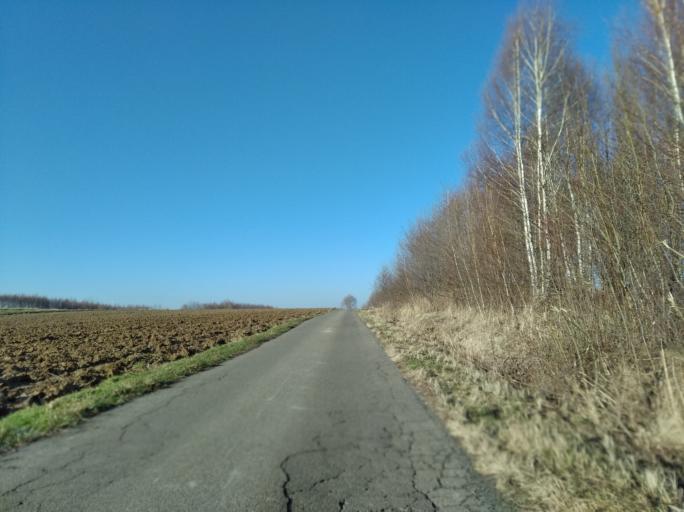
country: PL
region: Subcarpathian Voivodeship
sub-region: Powiat strzyzowski
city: Wysoka Strzyzowska
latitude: 49.8515
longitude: 21.7499
